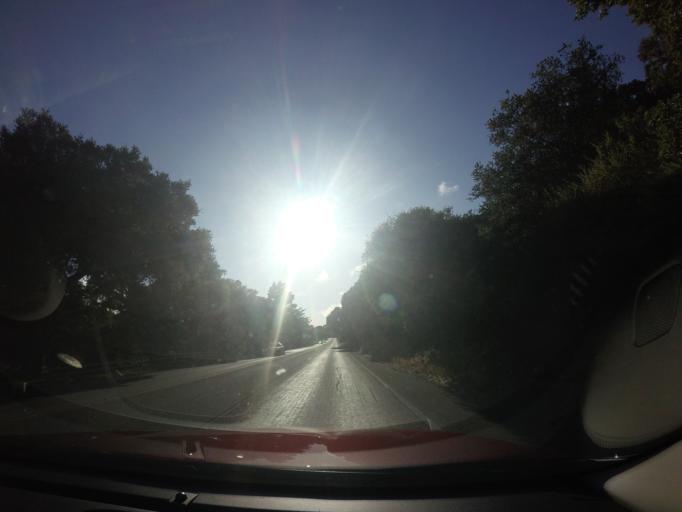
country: US
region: California
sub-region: Monterey County
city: Del Rey Oaks
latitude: 36.5334
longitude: -121.8453
